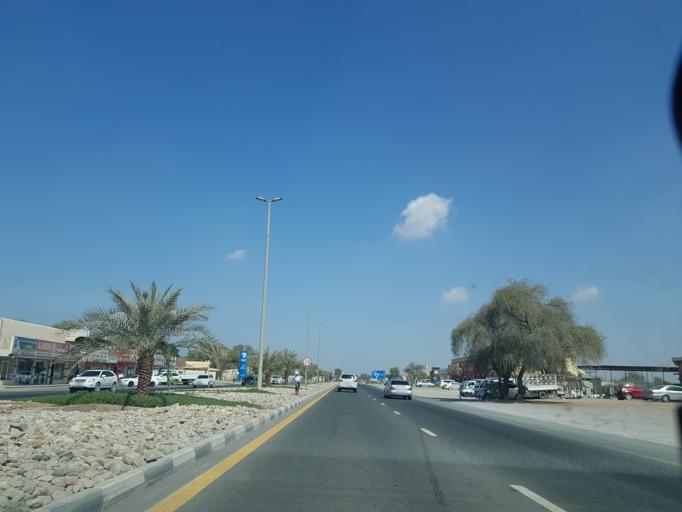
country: AE
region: Ra's al Khaymah
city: Ras al-Khaimah
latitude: 25.7086
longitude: 55.9699
